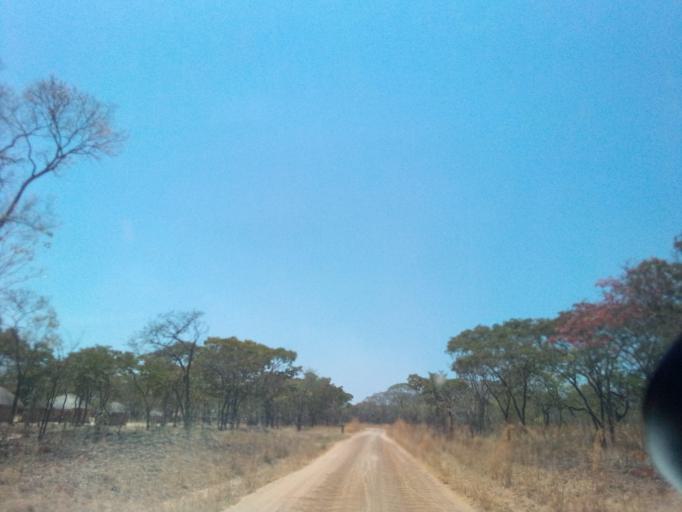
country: ZM
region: Northern
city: Mpika
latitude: -12.2537
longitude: 30.6932
